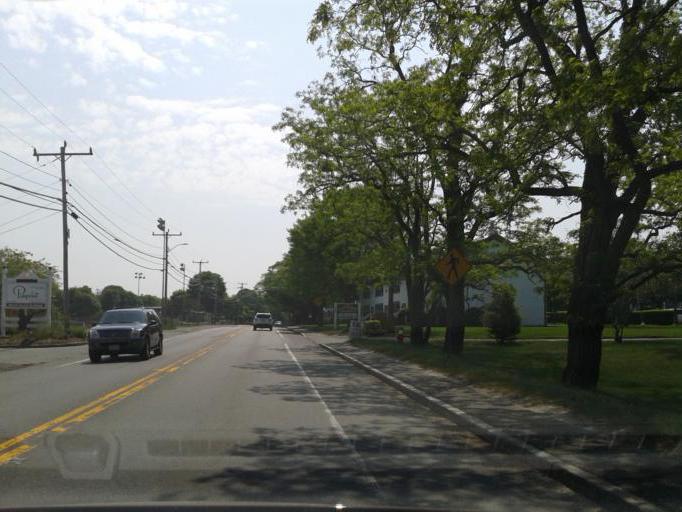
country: US
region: Massachusetts
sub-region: Barnstable County
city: Sagamore
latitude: 41.7739
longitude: -70.5419
